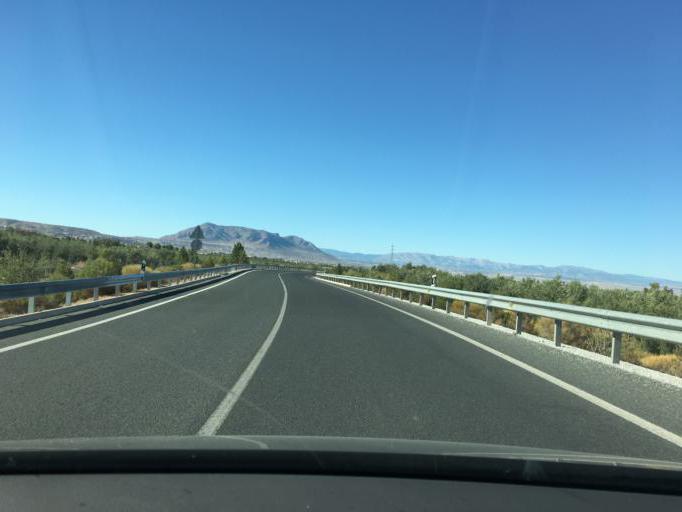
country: ES
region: Andalusia
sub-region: Provincia de Granada
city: Caniles
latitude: 37.4560
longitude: -2.7368
